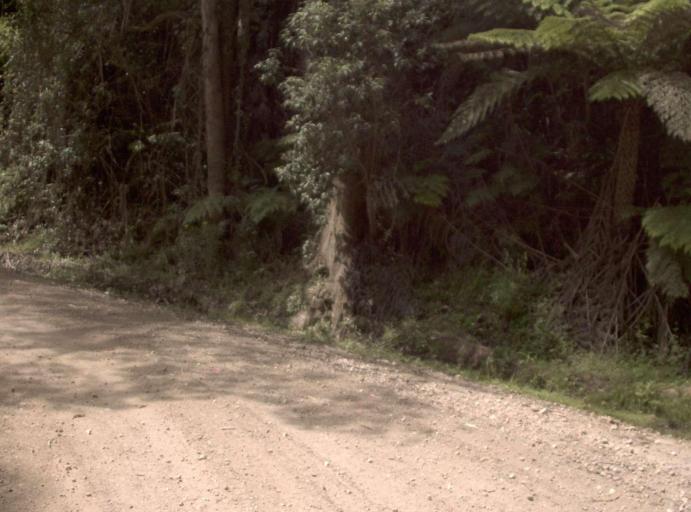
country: AU
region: Victoria
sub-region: East Gippsland
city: Lakes Entrance
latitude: -37.6144
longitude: 148.7022
